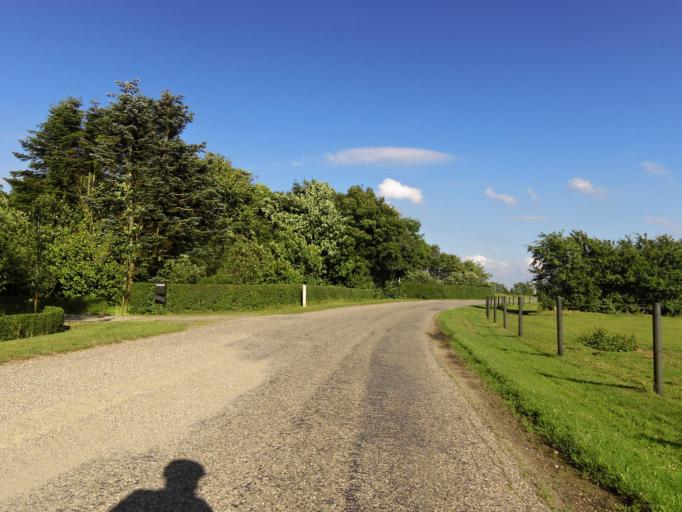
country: DK
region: South Denmark
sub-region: Vejen Kommune
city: Rodding
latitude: 55.3417
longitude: 9.1487
